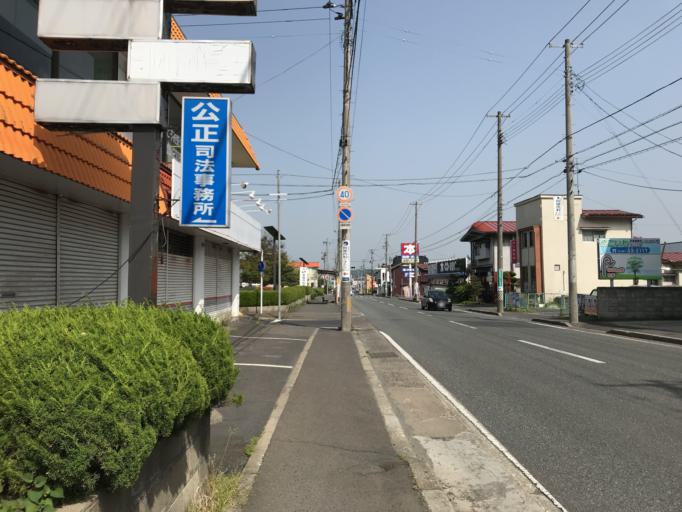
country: JP
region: Iwate
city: Ichinoseki
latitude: 38.9340
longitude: 141.1258
